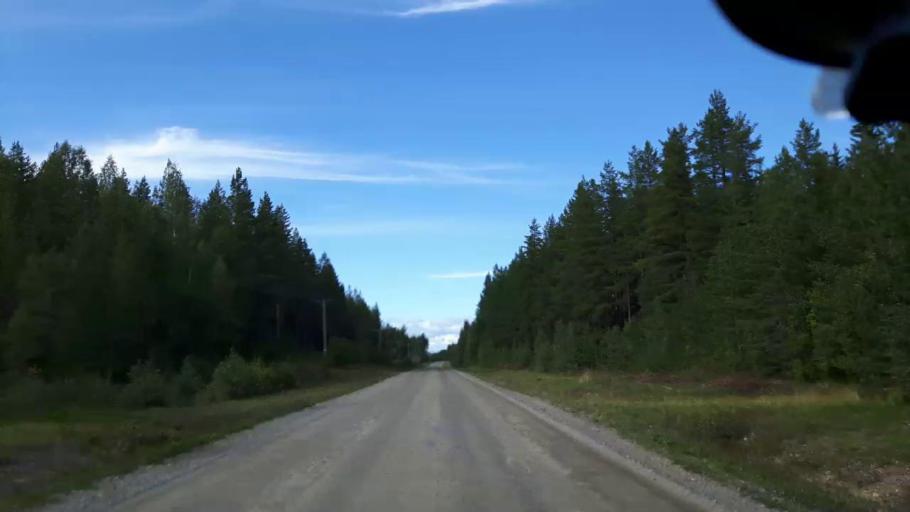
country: SE
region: Jaemtland
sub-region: Ragunda Kommun
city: Hammarstrand
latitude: 63.1387
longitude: 16.2367
